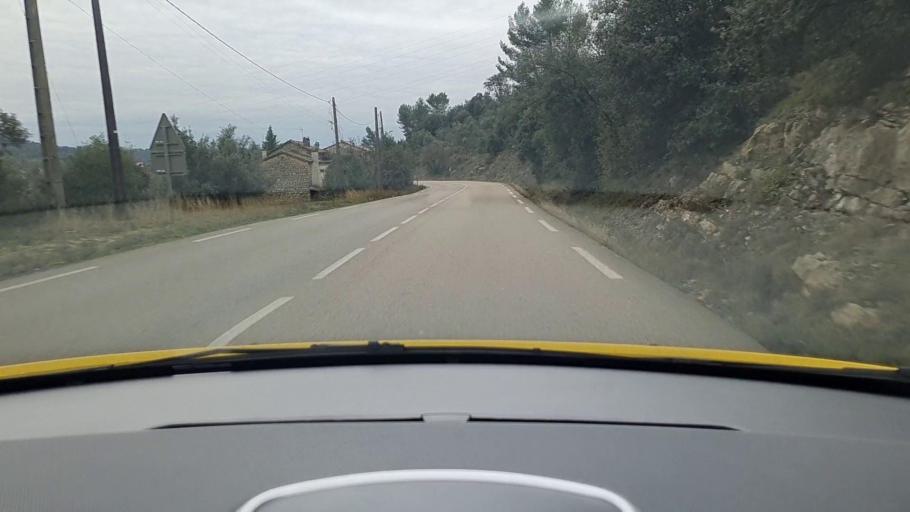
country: FR
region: Languedoc-Roussillon
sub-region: Departement du Gard
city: Saint-Martin-de-Valgalgues
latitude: 44.1699
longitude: 4.0836
